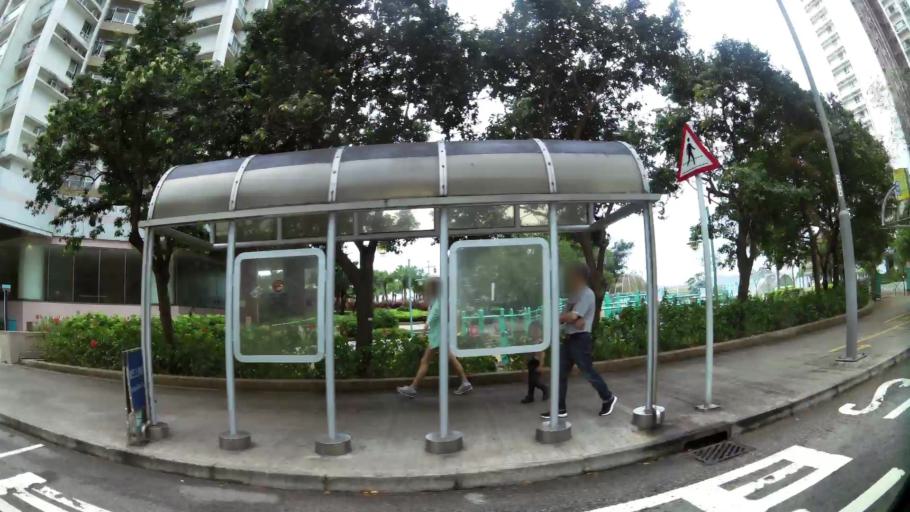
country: HK
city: Yung Shue Wan
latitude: 22.2432
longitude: 114.1473
